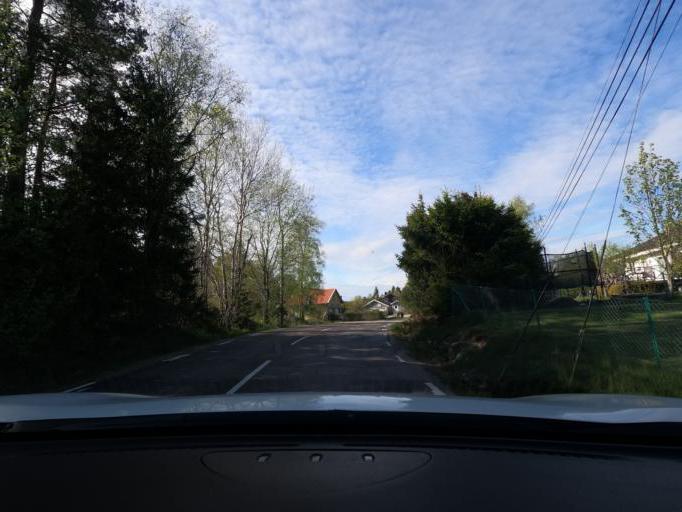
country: SE
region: Vaestra Goetaland
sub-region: Harryda Kommun
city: Landvetter
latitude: 57.6702
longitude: 12.2431
